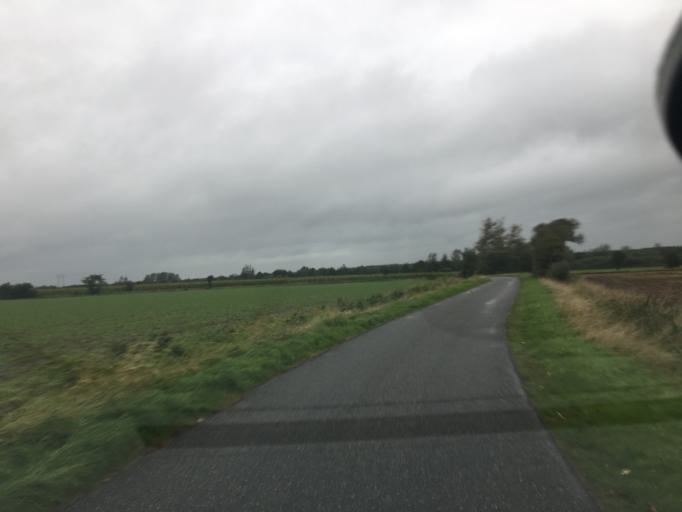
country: DE
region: Schleswig-Holstein
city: Ellhoft
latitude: 54.9381
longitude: 8.9514
